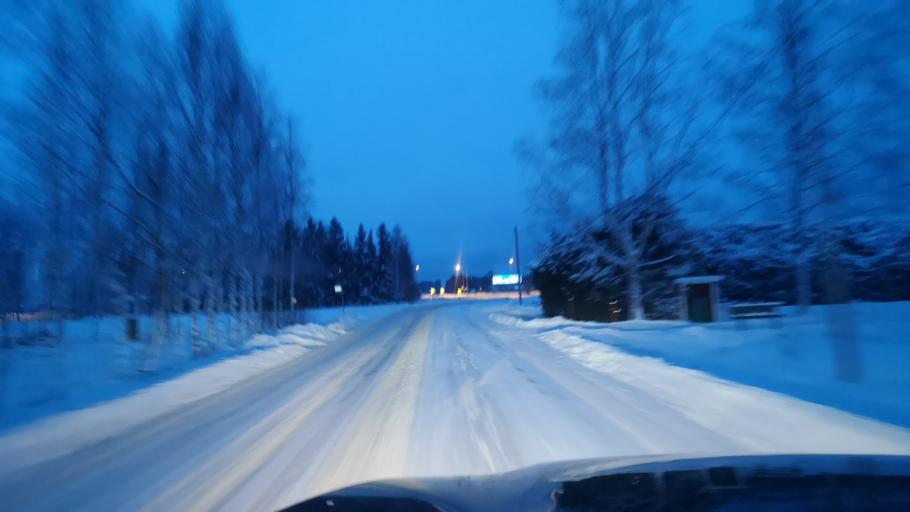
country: FI
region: Varsinais-Suomi
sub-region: Loimaa
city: Loimaa
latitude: 60.8825
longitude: 23.0892
